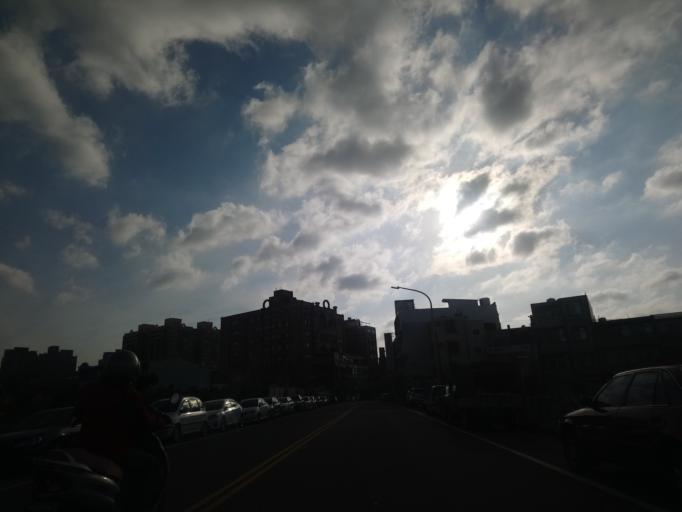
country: TW
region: Taiwan
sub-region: Hsinchu
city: Hsinchu
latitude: 24.7992
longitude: 120.9452
